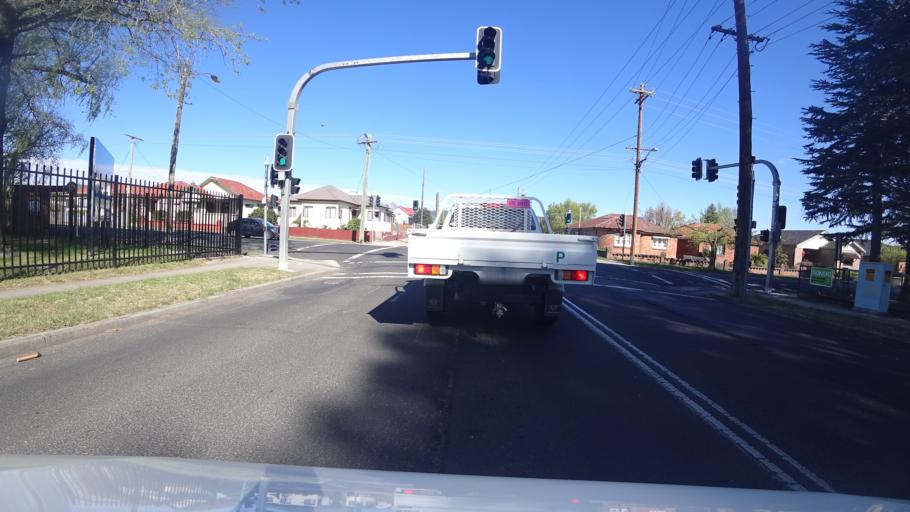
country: AU
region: New South Wales
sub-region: Lithgow
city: Lithgow
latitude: -33.4872
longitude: 150.1403
